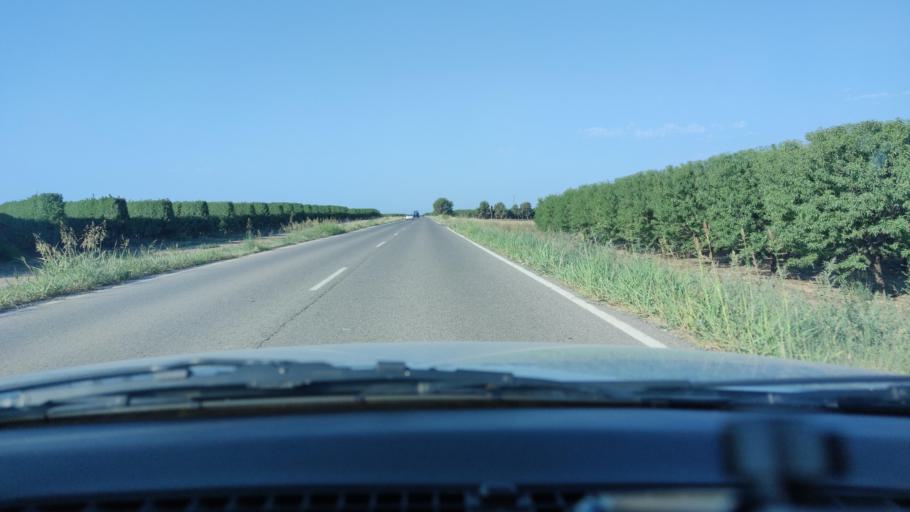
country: ES
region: Catalonia
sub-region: Provincia de Lleida
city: Balaguer
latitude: 41.8175
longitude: 0.8369
